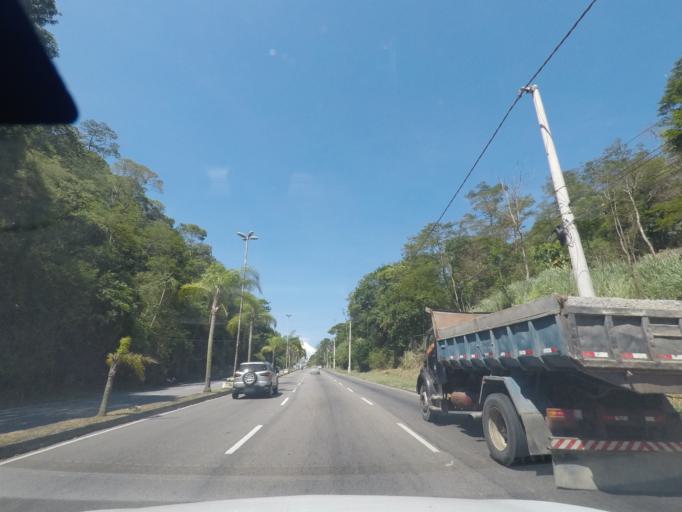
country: BR
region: Rio de Janeiro
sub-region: Niteroi
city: Niteroi
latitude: -22.9228
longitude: -43.0566
